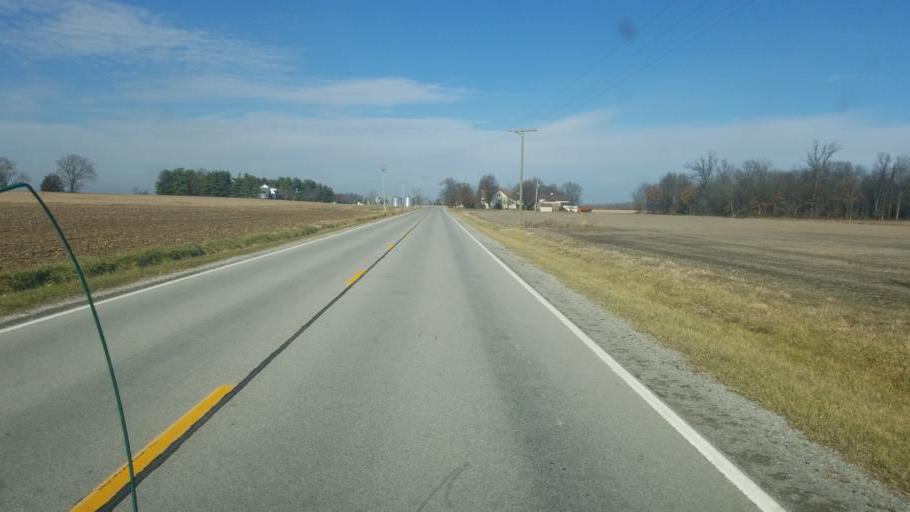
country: US
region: Illinois
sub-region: Saline County
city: Eldorado
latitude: 37.8964
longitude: -88.4530
